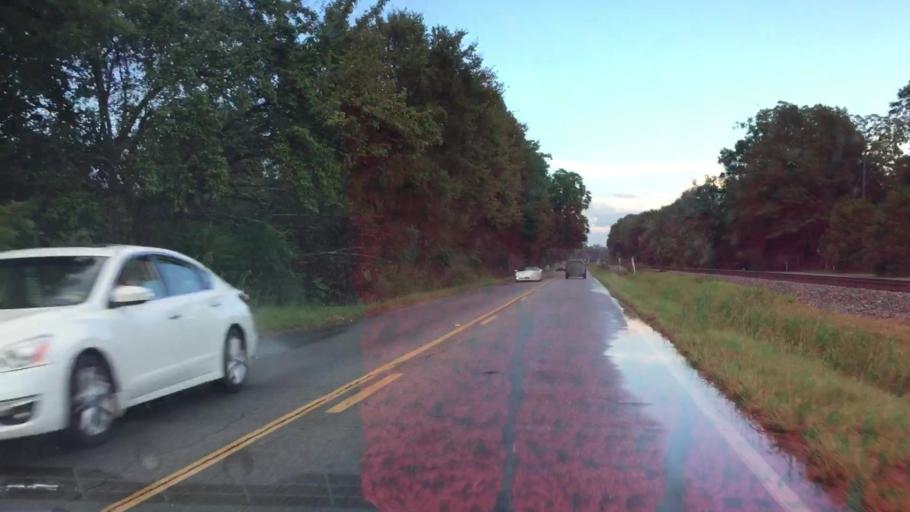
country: US
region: Georgia
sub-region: Clayton County
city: Lovejoy
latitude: 33.4335
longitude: -84.3032
